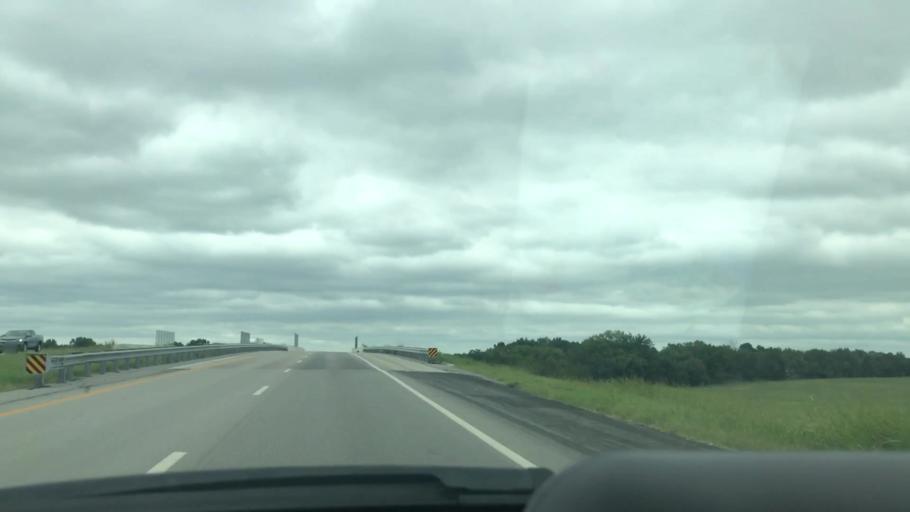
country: US
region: Oklahoma
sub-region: Mayes County
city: Pryor
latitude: 36.3716
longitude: -95.2940
